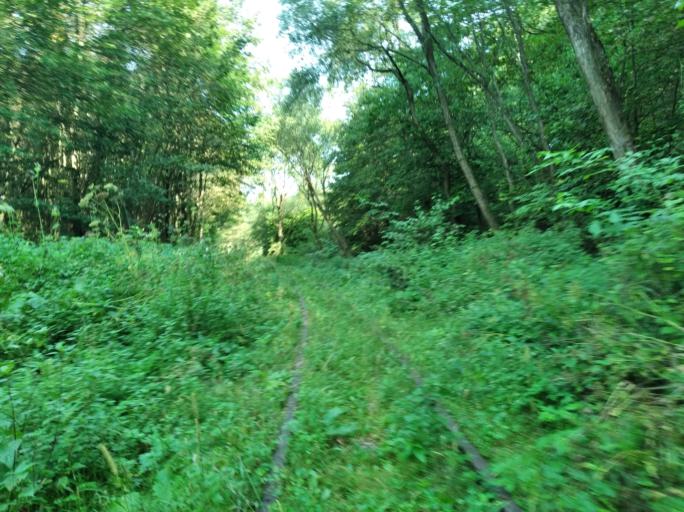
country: PL
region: Subcarpathian Voivodeship
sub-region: Powiat przeworski
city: Jawornik Polski
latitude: 49.8865
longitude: 22.2516
